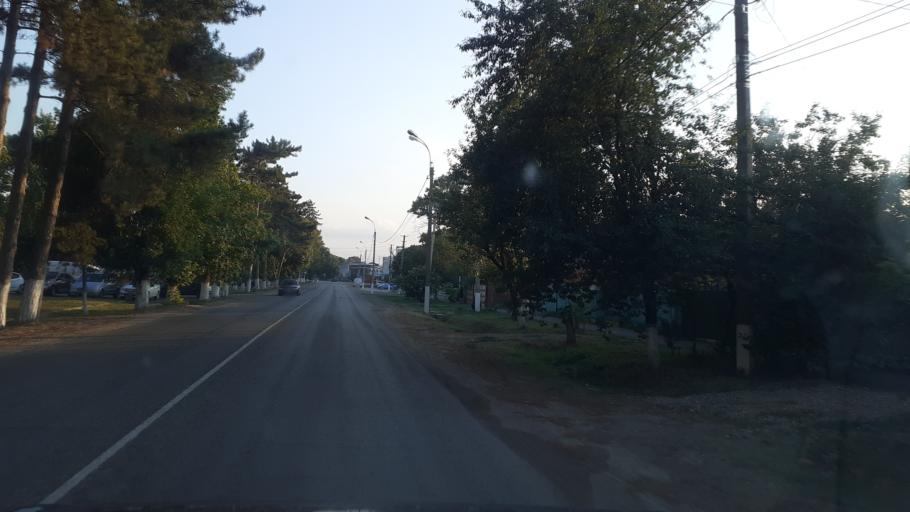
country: RU
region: Krasnodarskiy
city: Severskaya
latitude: 44.8535
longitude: 38.6788
